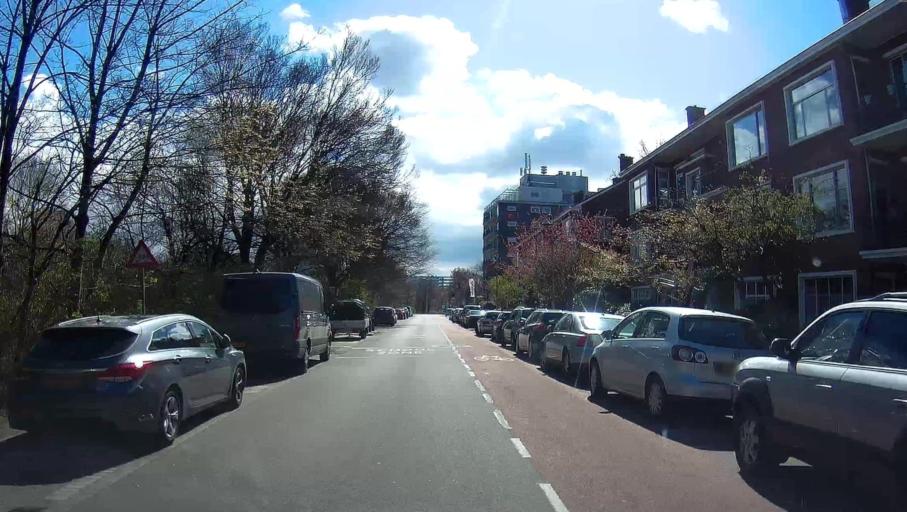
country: NL
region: South Holland
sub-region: Gemeente Den Haag
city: Scheveningen
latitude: 52.0713
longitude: 4.2419
